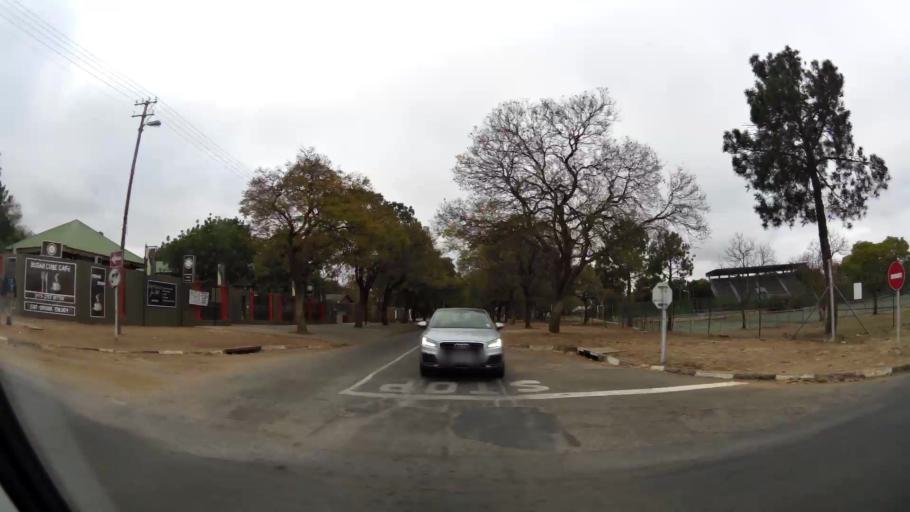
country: ZA
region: Limpopo
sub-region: Capricorn District Municipality
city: Polokwane
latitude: -23.9005
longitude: 29.4614
